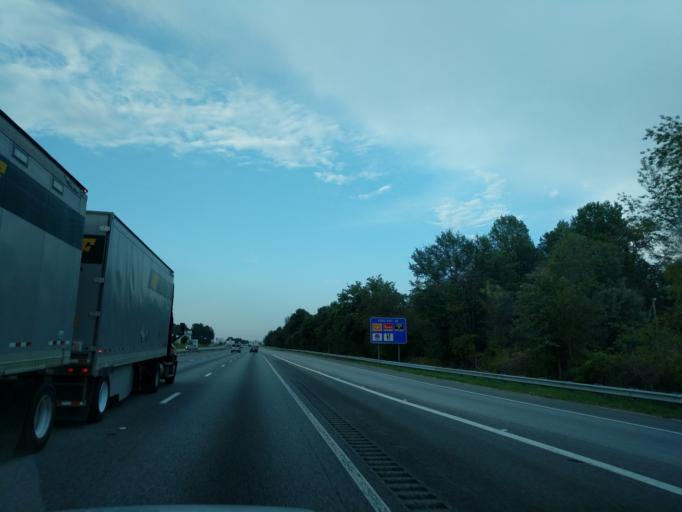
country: US
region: South Carolina
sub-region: Anderson County
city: Powdersville
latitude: 34.7607
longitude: -82.4739
